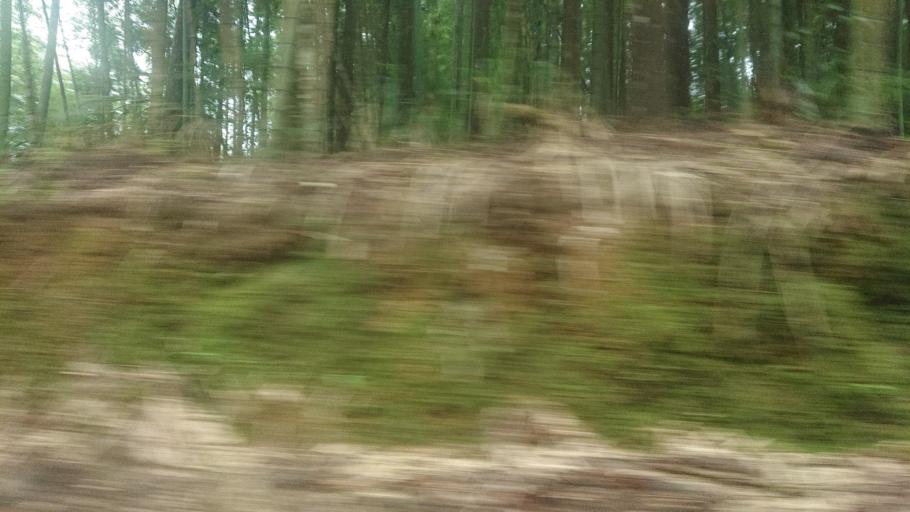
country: TW
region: Taiwan
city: Lugu
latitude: 23.6248
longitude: 120.7163
